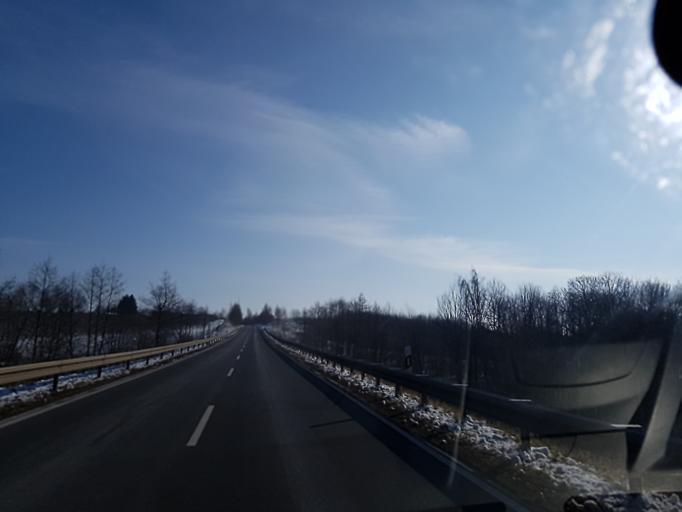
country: DE
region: Saxony
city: Leisnig
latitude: 51.1509
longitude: 12.9192
